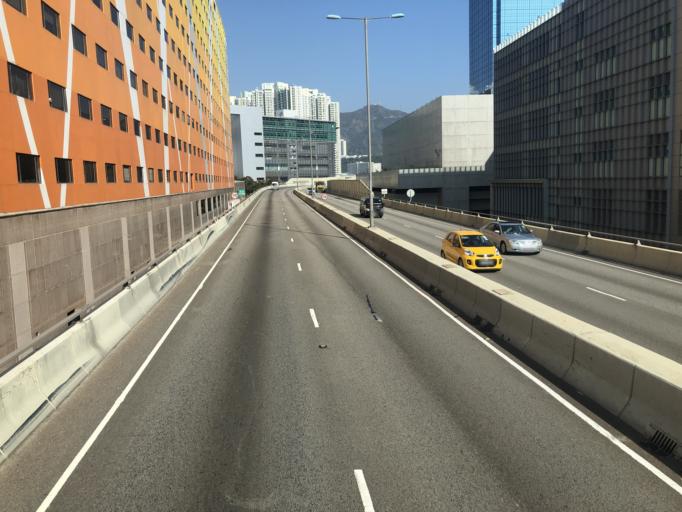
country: HK
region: Kowloon City
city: Kowloon
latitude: 22.3229
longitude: 114.2044
